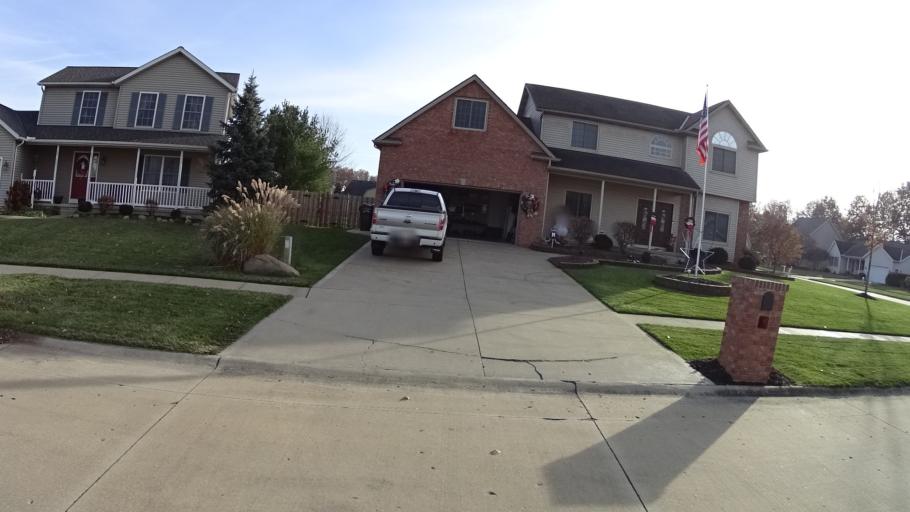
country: US
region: Ohio
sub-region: Lorain County
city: Elyria
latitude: 41.3382
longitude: -82.0769
